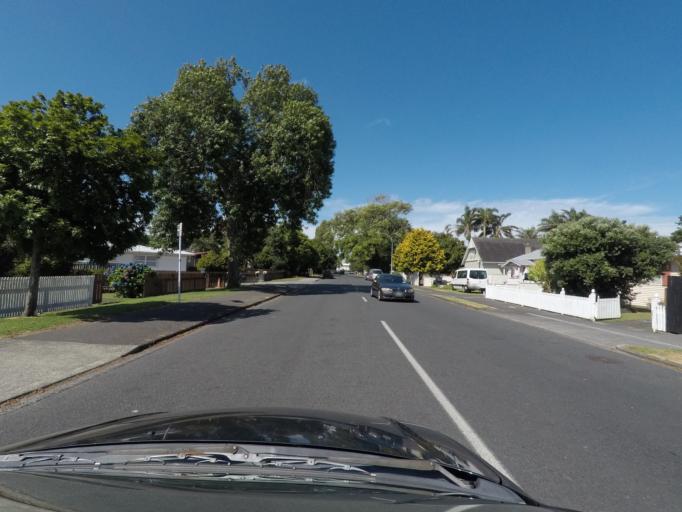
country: NZ
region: Auckland
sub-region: Auckland
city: Rosebank
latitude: -36.8854
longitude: 174.6805
